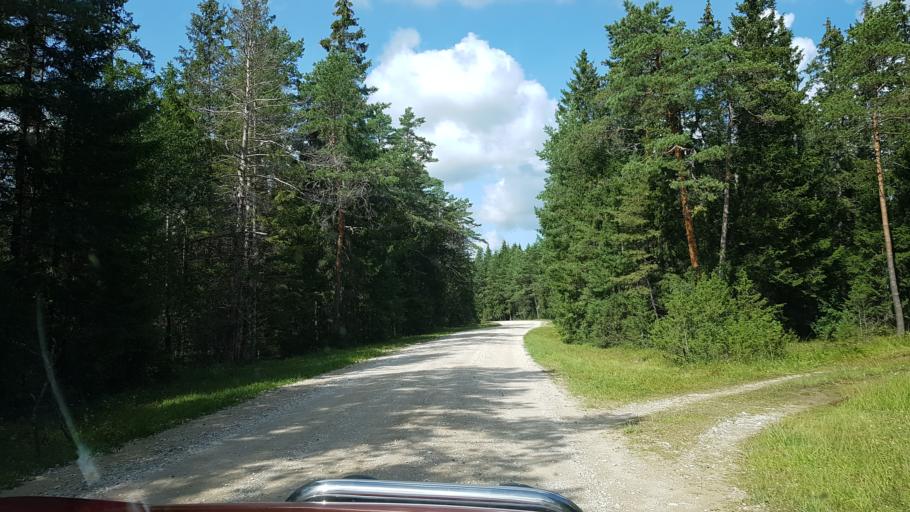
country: EE
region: Raplamaa
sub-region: Rapla vald
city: Rapla
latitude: 58.9647
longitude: 24.6373
